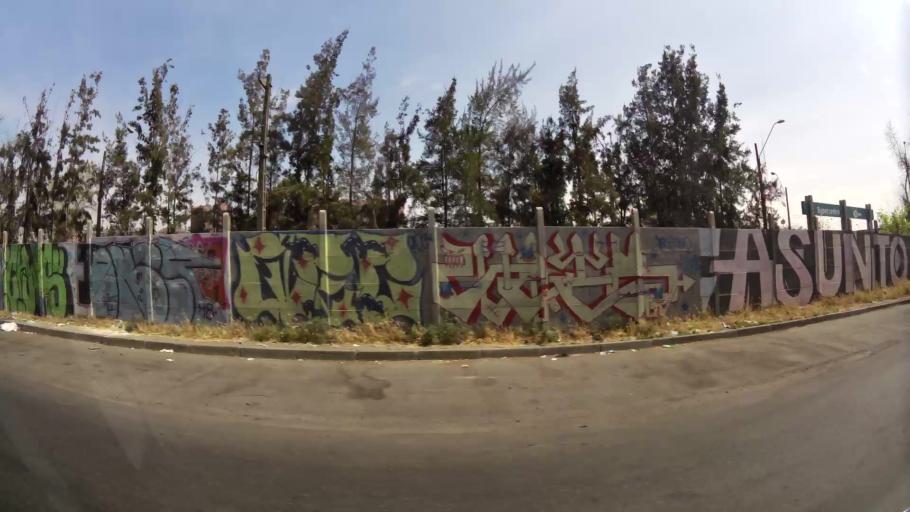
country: CL
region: Santiago Metropolitan
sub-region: Provincia de Santiago
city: Santiago
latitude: -33.4293
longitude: -70.6808
